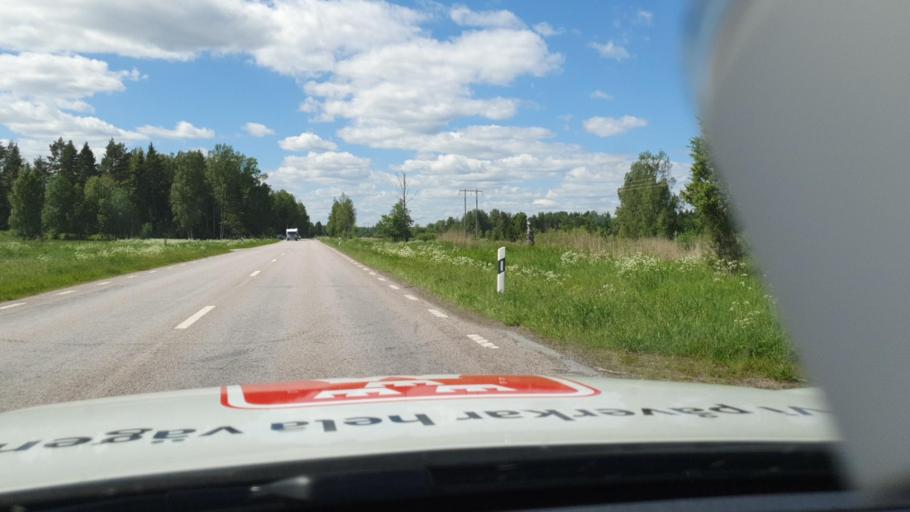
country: SE
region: Uppsala
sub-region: Tierps Kommun
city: Karlholmsbruk
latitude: 60.5007
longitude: 17.6770
